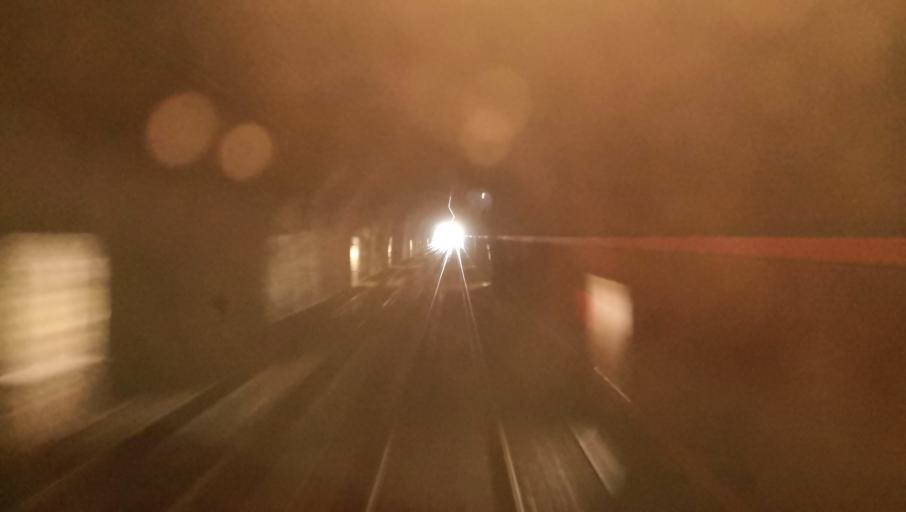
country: FR
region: Ile-de-France
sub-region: Departement des Yvelines
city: Longnes
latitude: 48.9550
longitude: 1.5739
